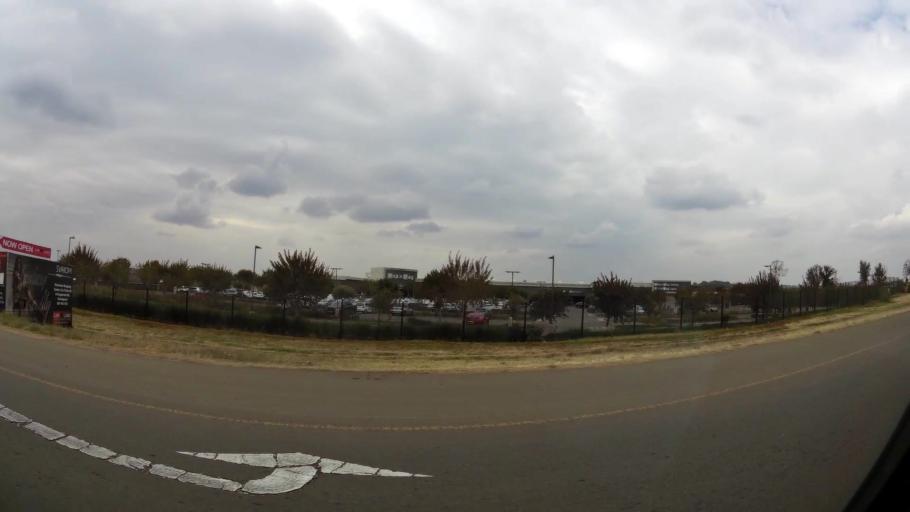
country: ZA
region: Gauteng
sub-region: City of Johannesburg Metropolitan Municipality
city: Roodepoort
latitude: -26.1098
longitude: 27.8847
